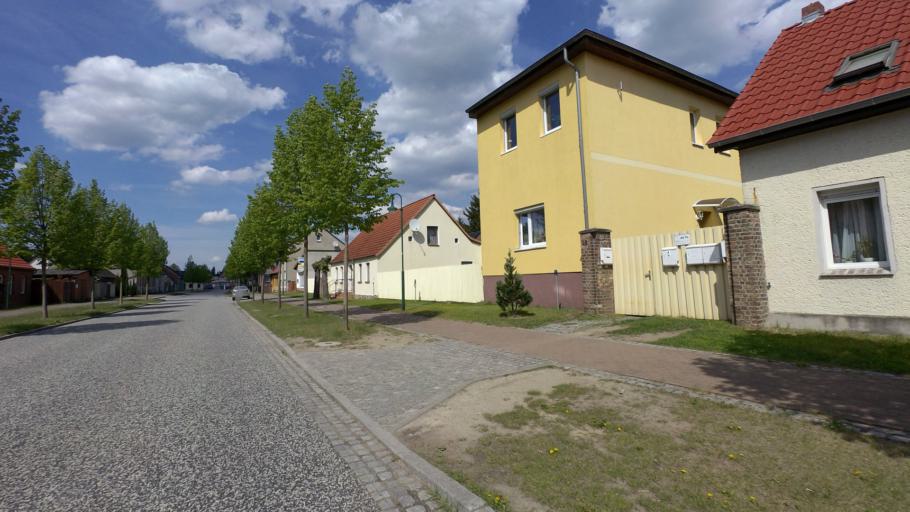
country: DE
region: Brandenburg
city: Marienwerder
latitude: 52.9027
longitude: 13.5351
